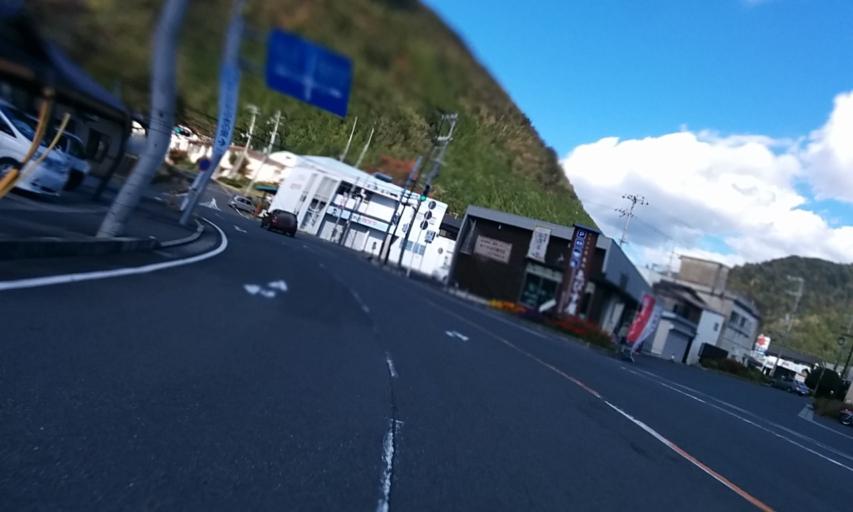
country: JP
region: Kyoto
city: Kameoka
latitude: 35.2749
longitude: 135.5514
